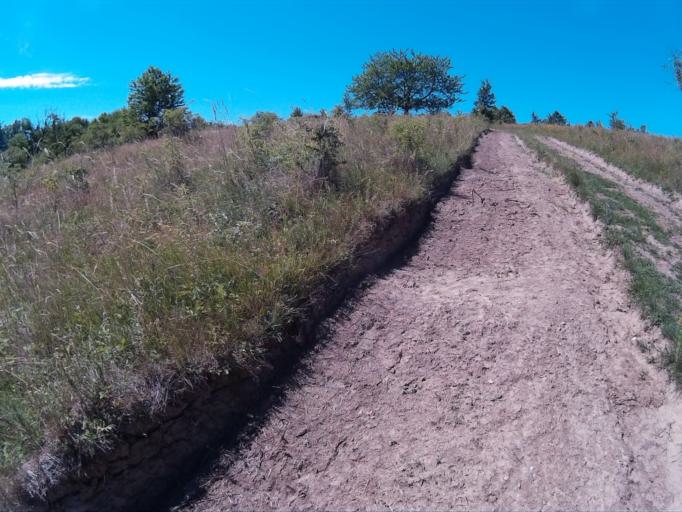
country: HU
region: Veszprem
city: Urkut
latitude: 47.1348
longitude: 17.6550
